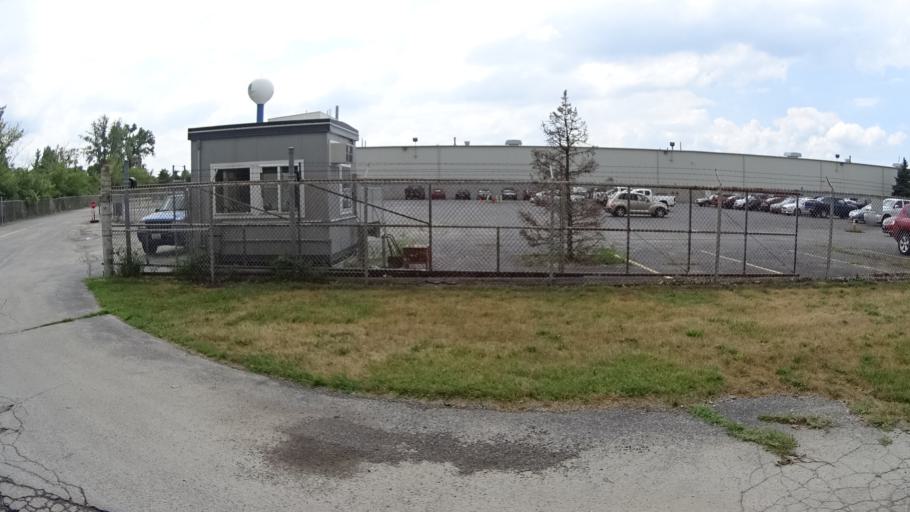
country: US
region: Ohio
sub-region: Erie County
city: Sandusky
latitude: 41.4443
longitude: -82.7407
